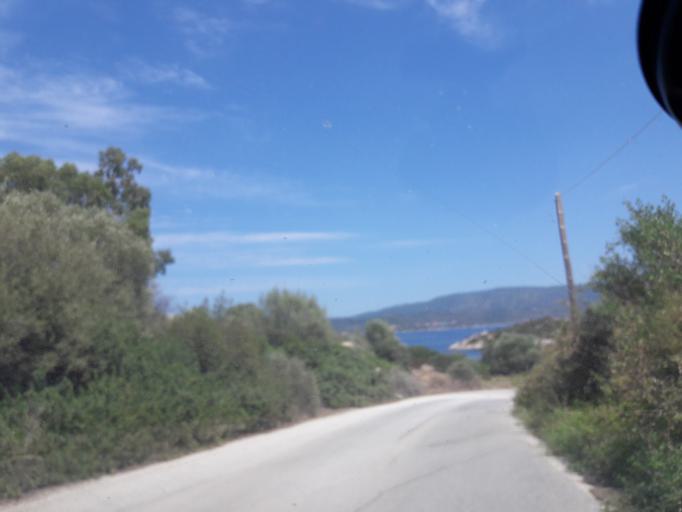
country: GR
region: Central Macedonia
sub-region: Nomos Chalkidikis
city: Ouranoupolis
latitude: 40.3165
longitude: 23.9314
